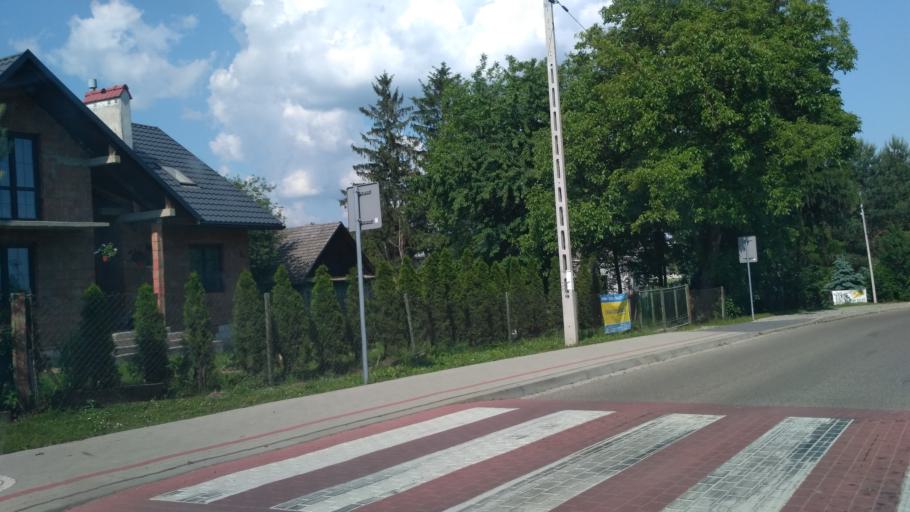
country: PL
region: Subcarpathian Voivodeship
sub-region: Powiat jaroslawski
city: Rokietnica
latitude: 49.9447
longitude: 22.6737
